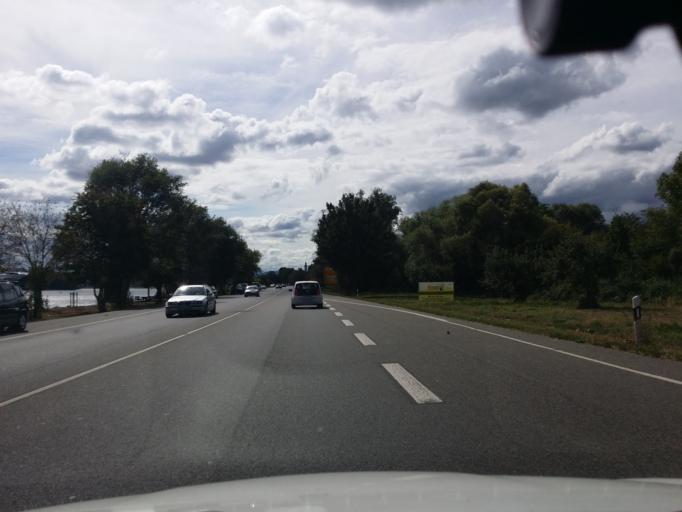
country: DE
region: Rheinland-Pfalz
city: Oestrich-Winkel
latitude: 50.0022
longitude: 8.0253
